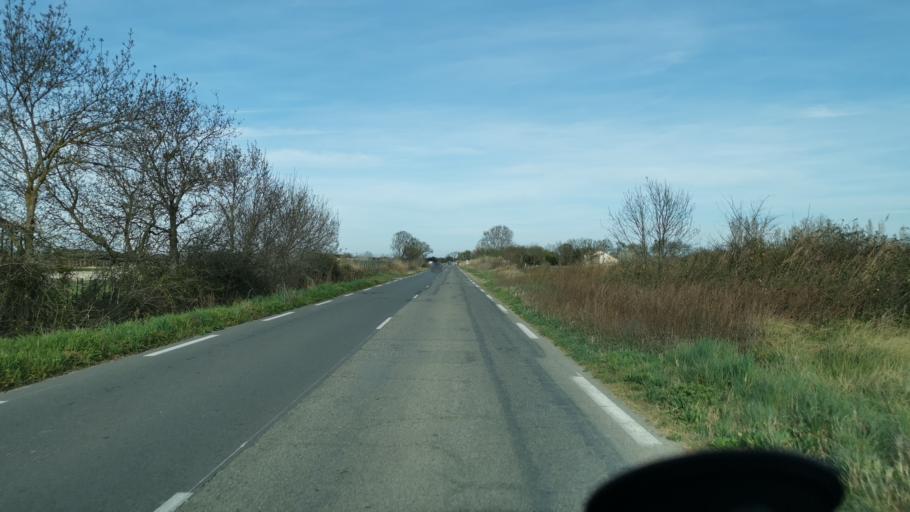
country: FR
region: Provence-Alpes-Cote d'Azur
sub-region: Departement des Bouches-du-Rhone
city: Saint-Martin-de-Crau
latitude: 43.5617
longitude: 4.7350
